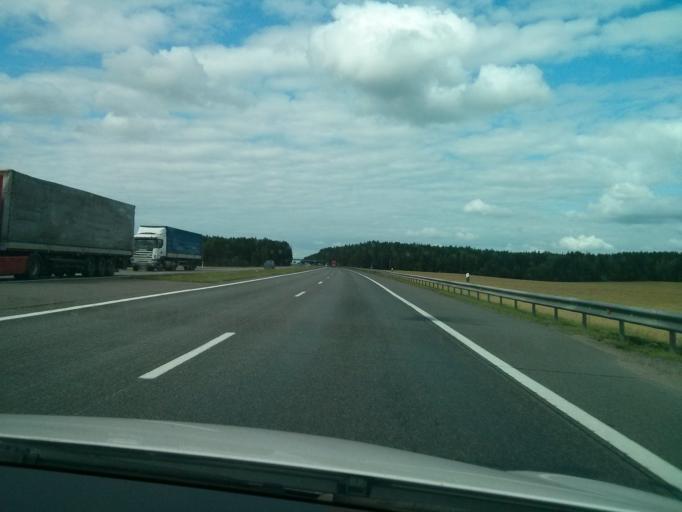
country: BY
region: Minsk
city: Zamostochcha
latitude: 53.8849
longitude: 27.9380
